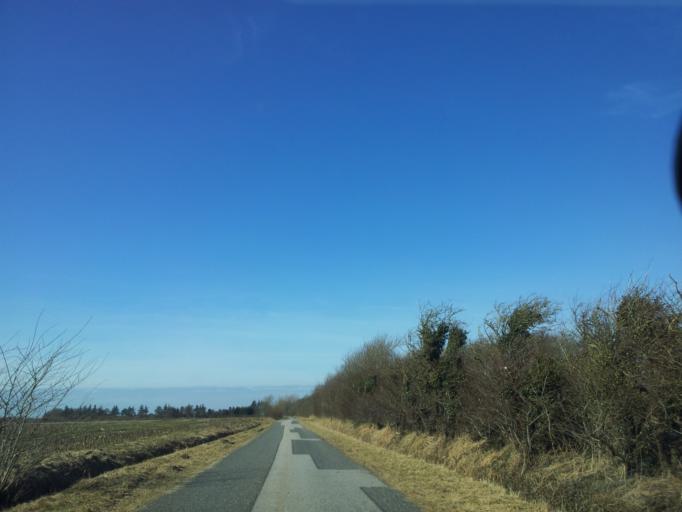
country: DK
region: South Denmark
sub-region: Tonder Kommune
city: Sherrebek
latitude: 55.2044
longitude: 8.7427
